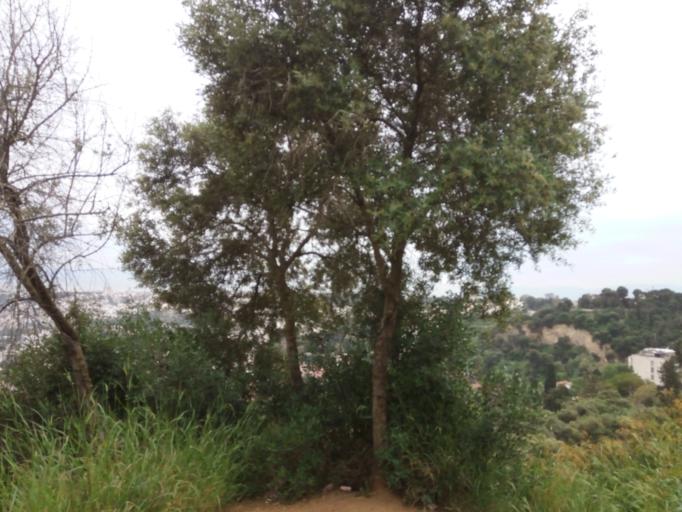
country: DZ
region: Alger
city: Algiers
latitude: 36.7676
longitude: 3.0394
